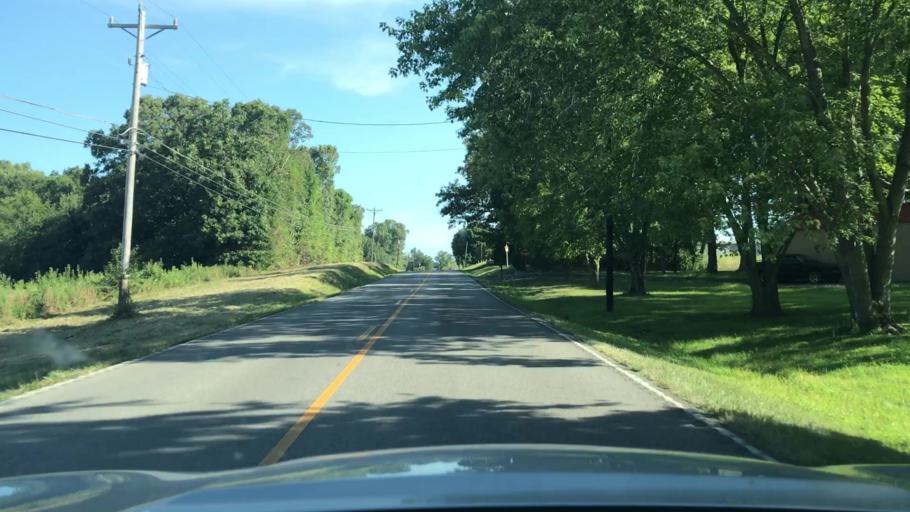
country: US
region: Kentucky
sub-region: Muhlenberg County
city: Greenville
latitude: 37.1539
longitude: -87.1417
